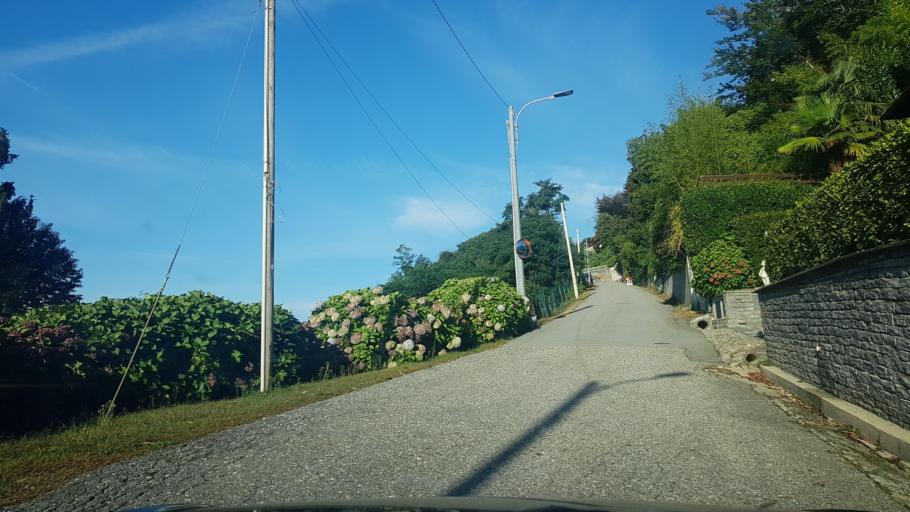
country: IT
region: Piedmont
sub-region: Provincia Verbano-Cusio-Ossola
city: Bee
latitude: 45.9652
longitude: 8.5790
